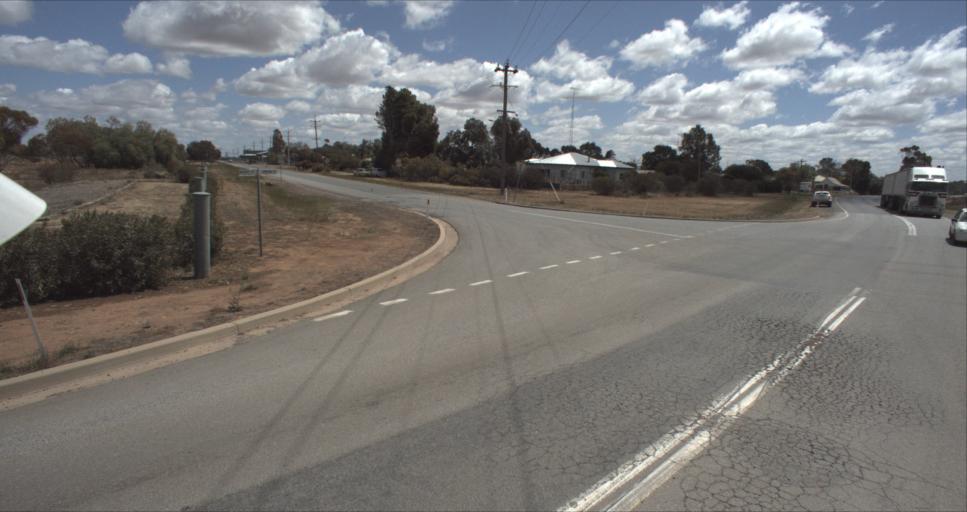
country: AU
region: New South Wales
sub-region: Murrumbidgee Shire
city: Darlington Point
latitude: -34.5168
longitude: 146.1855
